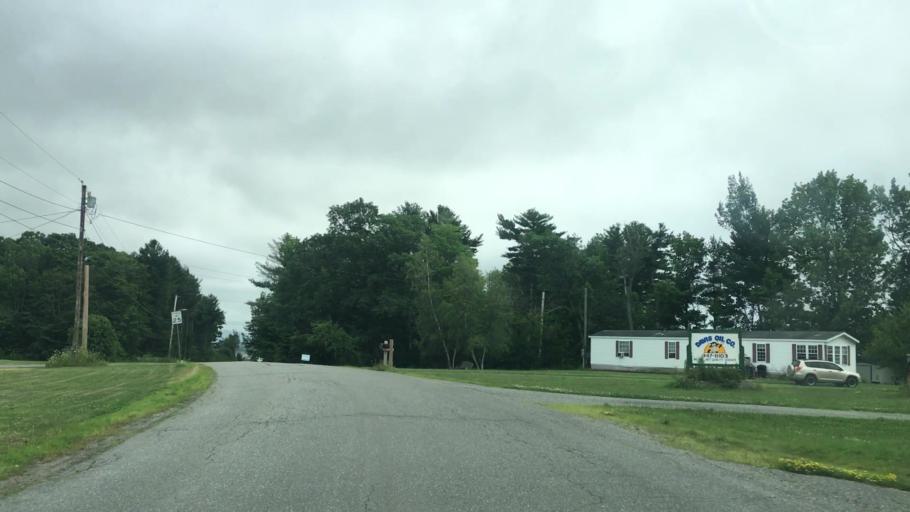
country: US
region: Maine
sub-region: Penobscot County
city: Veazie
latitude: 44.8472
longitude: -68.7470
